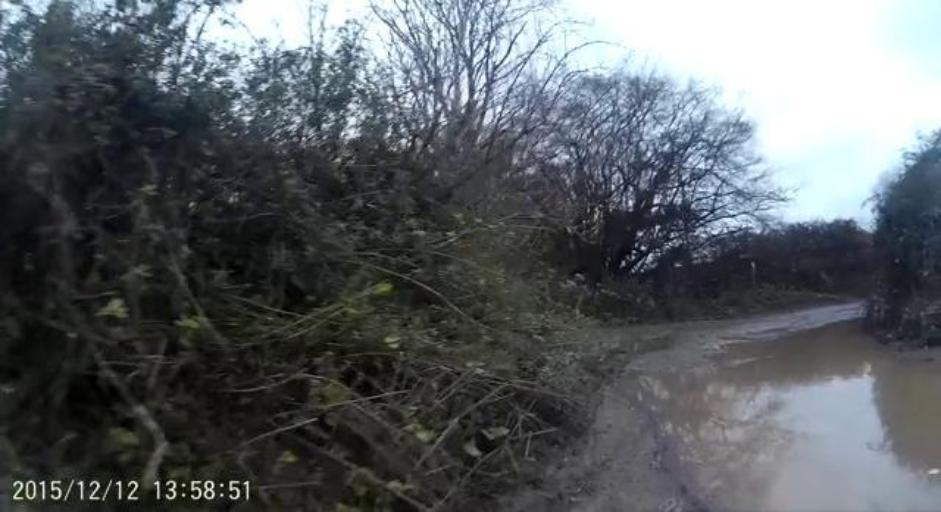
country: GB
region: England
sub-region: West Sussex
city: Milland
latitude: 50.9629
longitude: -0.8401
